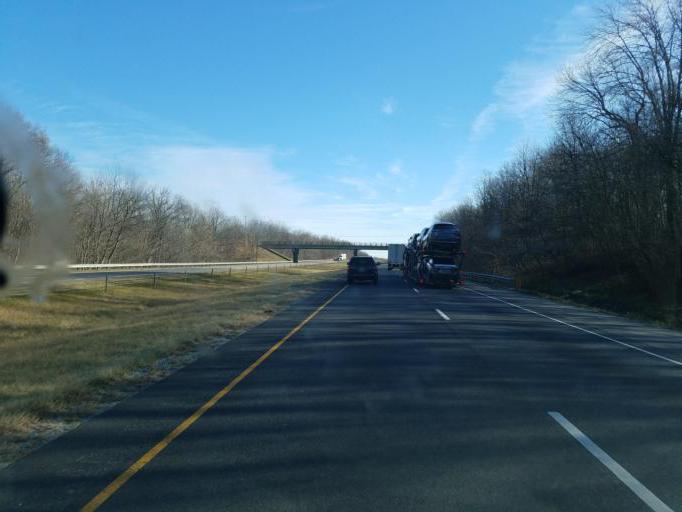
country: US
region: Indiana
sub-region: Henry County
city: Knightstown
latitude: 39.8540
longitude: -85.4589
